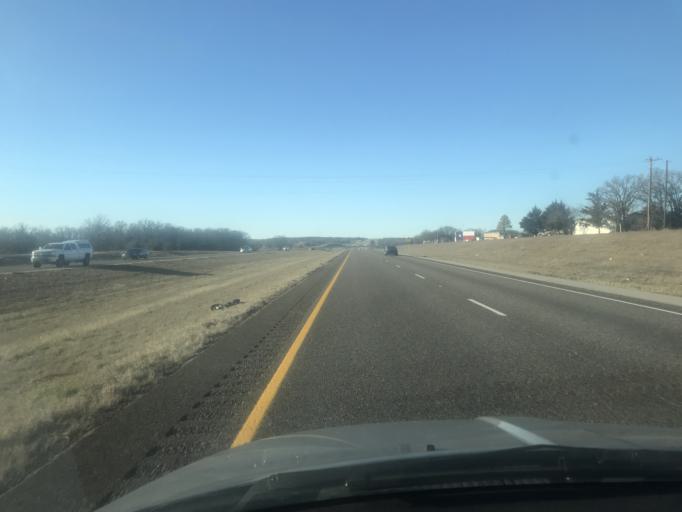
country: US
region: Texas
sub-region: Montague County
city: Bowie
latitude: 33.4846
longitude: -97.7969
